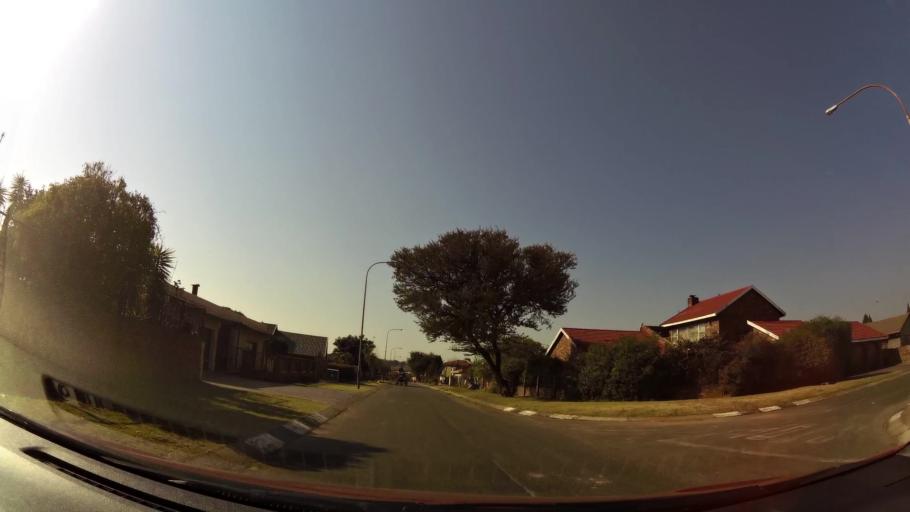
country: ZA
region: Gauteng
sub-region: City of Johannesburg Metropolitan Municipality
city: Johannesburg
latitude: -26.2485
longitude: 27.9598
